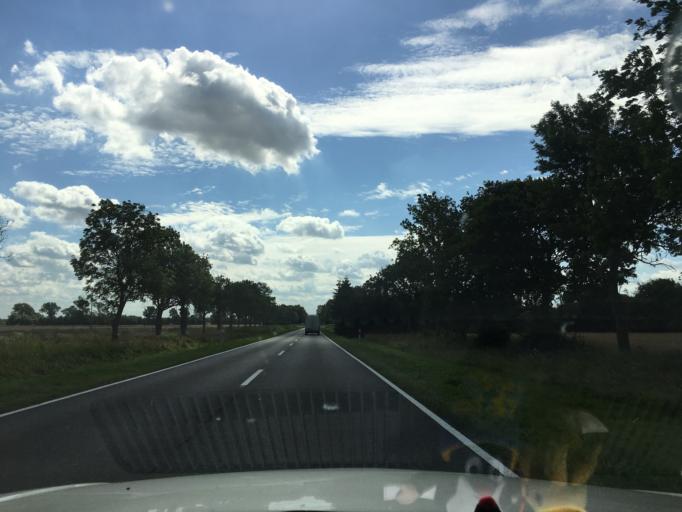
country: PL
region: West Pomeranian Voivodeship
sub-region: Powiat kamienski
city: Kamien Pomorski
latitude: 53.9483
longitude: 14.8025
